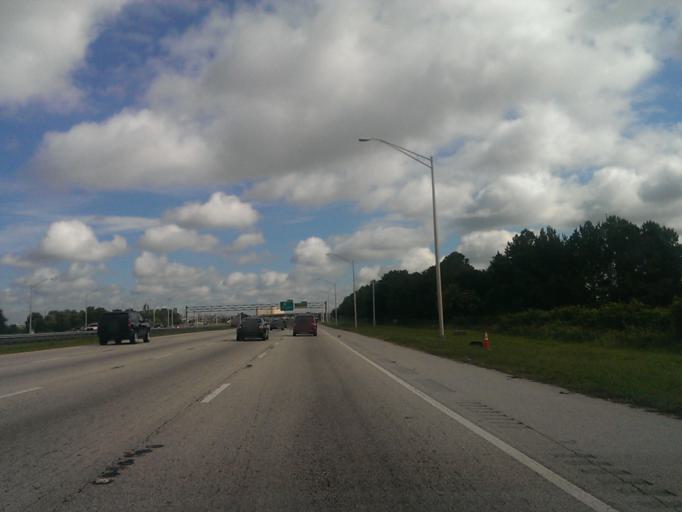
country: US
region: Florida
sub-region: Orange County
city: Williamsburg
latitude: 28.4024
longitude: -81.4820
